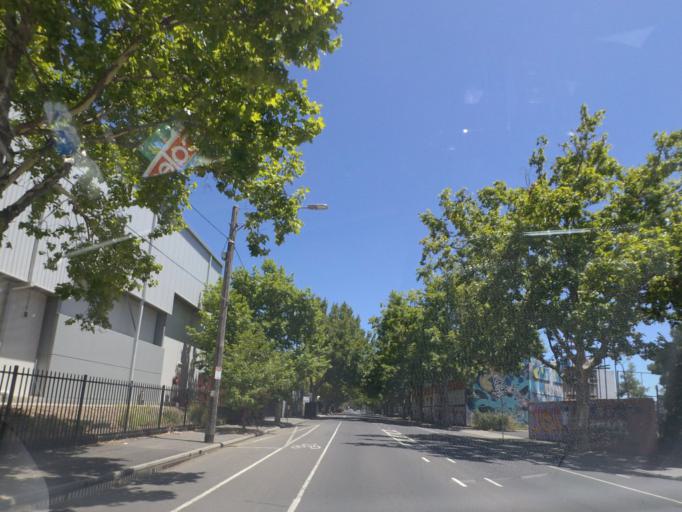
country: AU
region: Victoria
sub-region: Moonee Valley
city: Flemington
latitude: -37.7994
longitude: 144.9186
